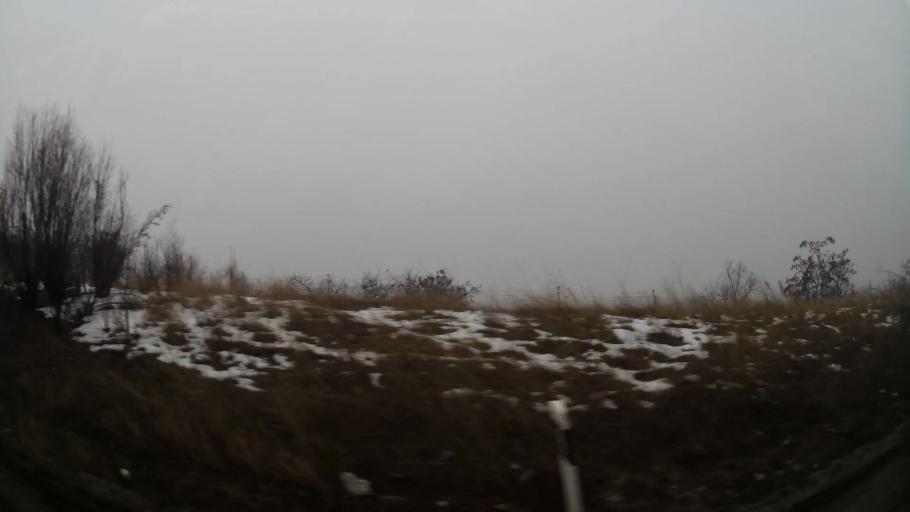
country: MK
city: Miladinovci
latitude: 41.9763
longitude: 21.6506
